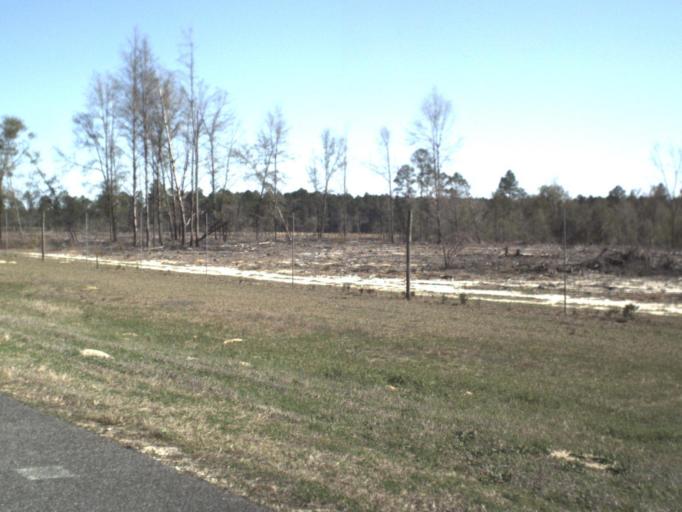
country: US
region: Florida
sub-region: Bay County
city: Youngstown
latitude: 30.4278
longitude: -85.5822
